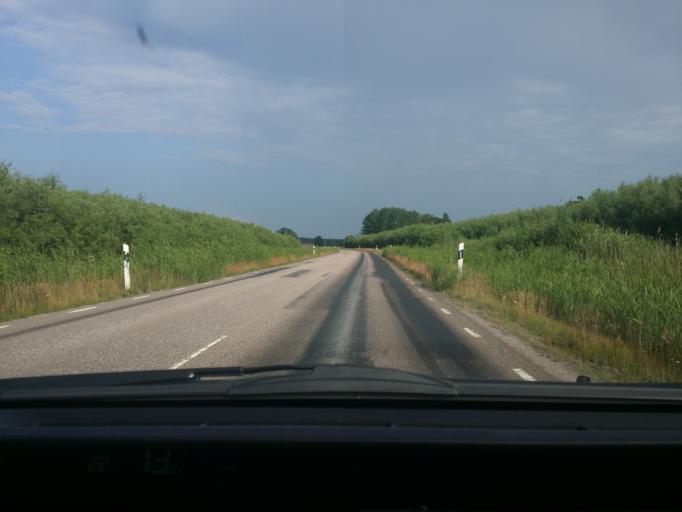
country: SE
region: Vaestmanland
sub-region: Hallstahammars Kommun
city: Kolback
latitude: 59.5593
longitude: 16.3272
